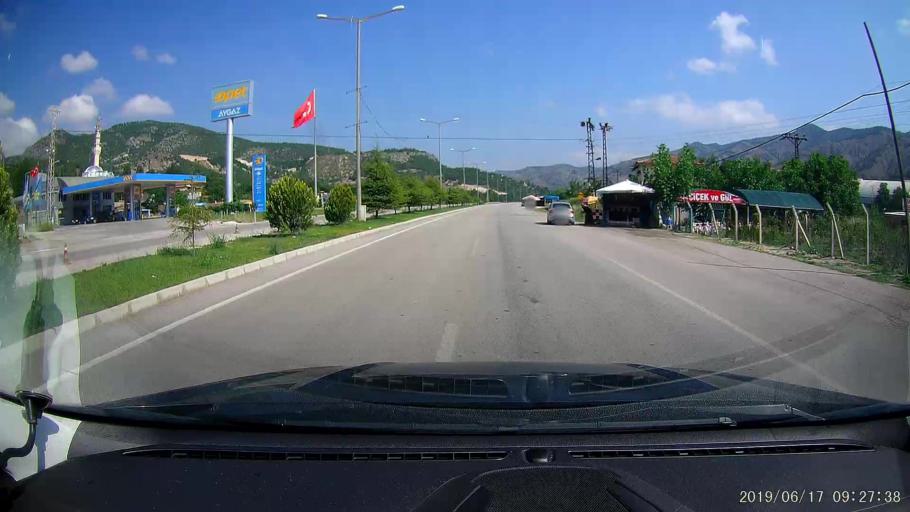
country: TR
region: Amasya
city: Amasya
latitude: 40.6792
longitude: 35.8251
